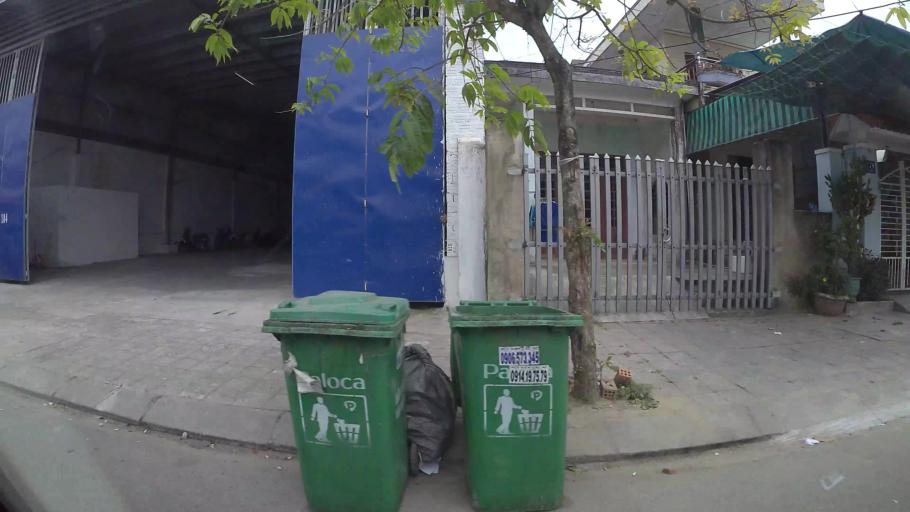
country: VN
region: Da Nang
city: Lien Chieu
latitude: 16.0637
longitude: 108.1668
